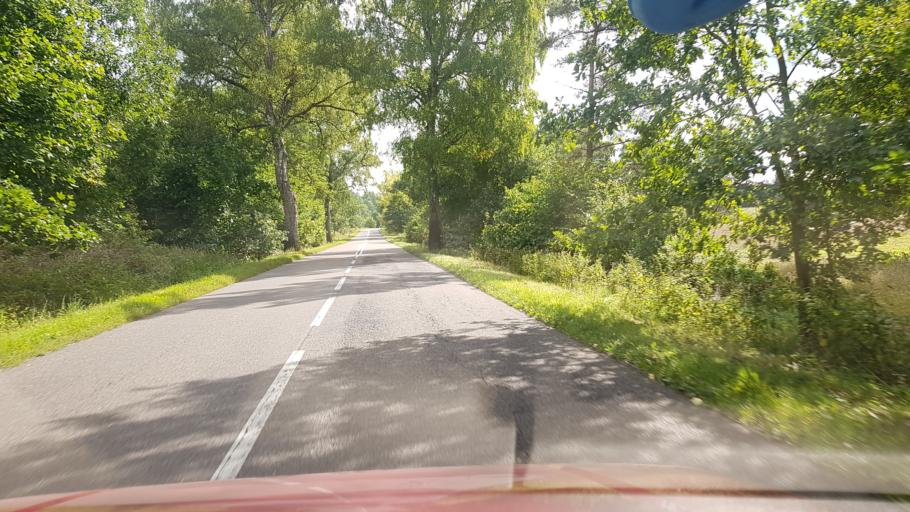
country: PL
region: West Pomeranian Voivodeship
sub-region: Powiat koszalinski
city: Polanow
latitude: 54.1170
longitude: 16.7504
